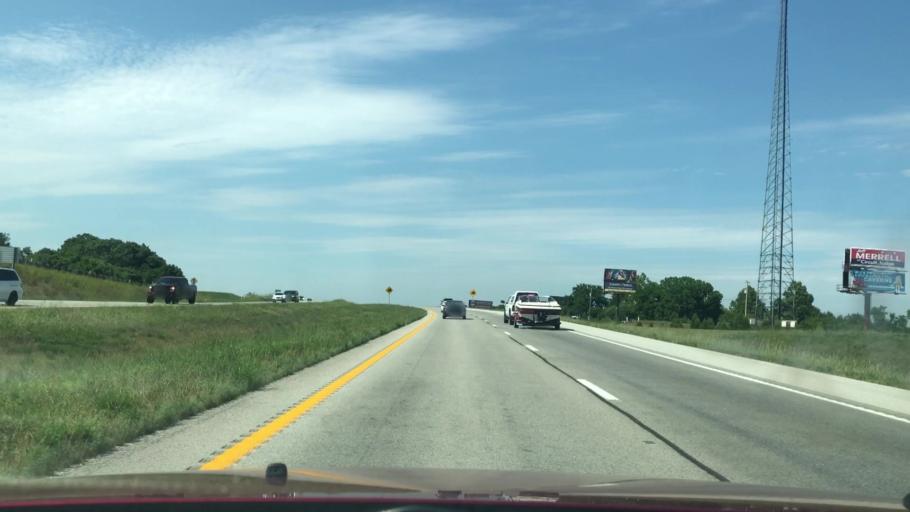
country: US
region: Missouri
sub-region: Taney County
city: Merriam Woods
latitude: 36.8064
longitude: -93.2254
